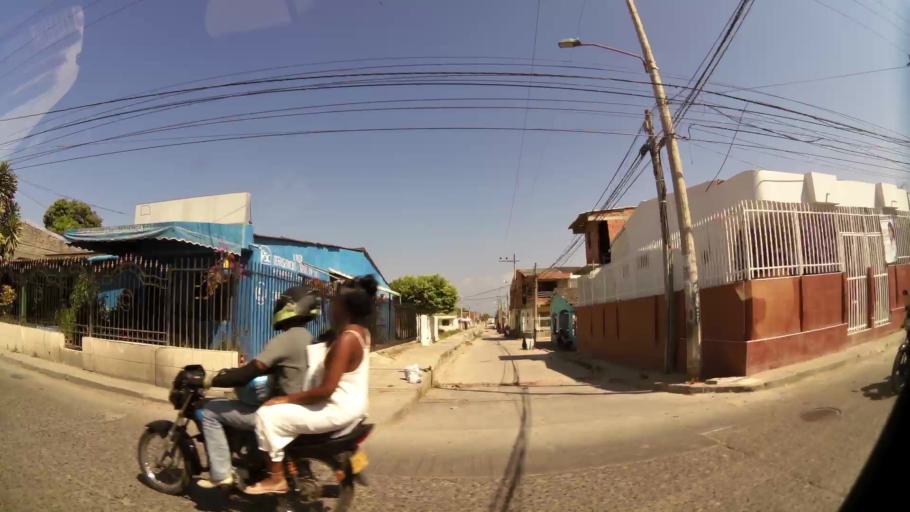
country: CO
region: Bolivar
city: Cartagena
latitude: 10.4185
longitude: -75.5197
